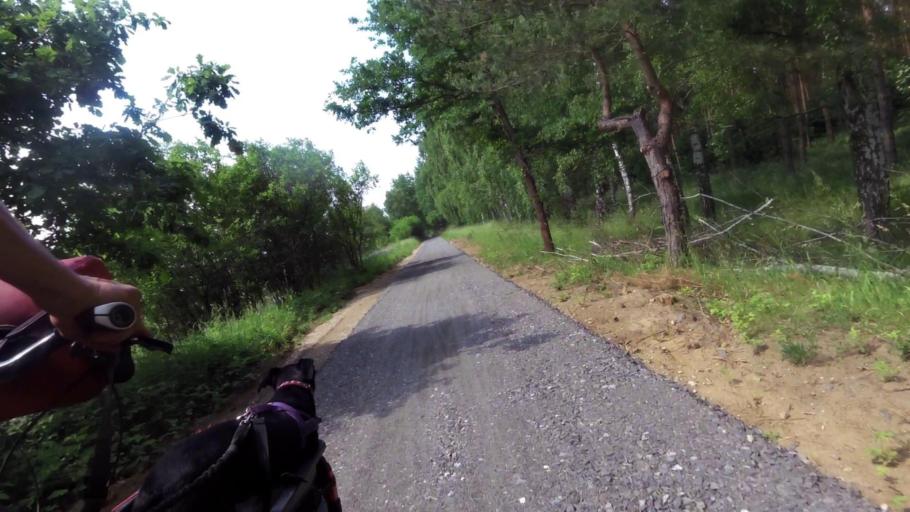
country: PL
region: West Pomeranian Voivodeship
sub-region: Powiat pyrzycki
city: Bielice
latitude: 53.2054
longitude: 14.6159
